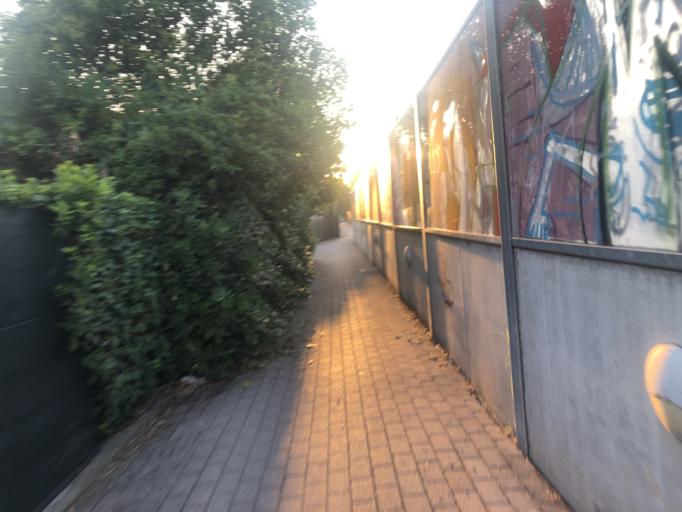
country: IT
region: Tuscany
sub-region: Province of Pisa
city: Pisa
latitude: 43.7238
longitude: 10.4122
